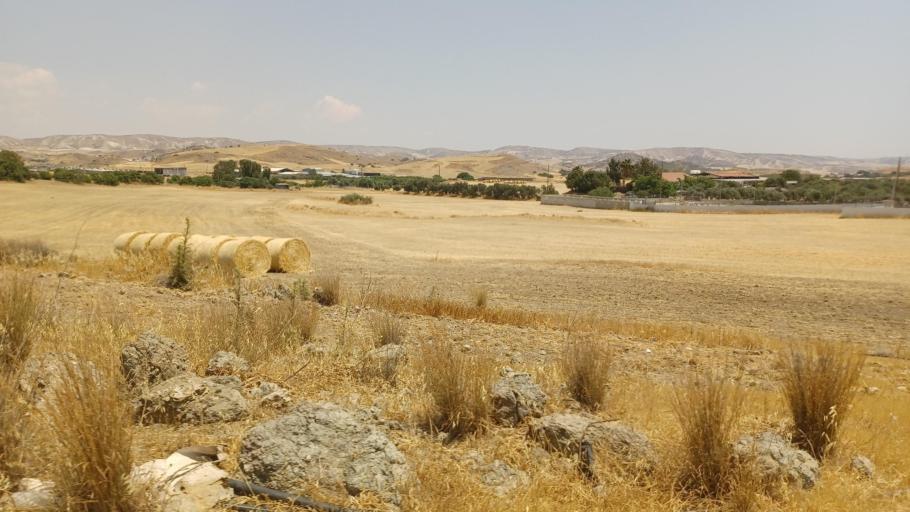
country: CY
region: Larnaka
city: Troulloi
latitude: 35.0138
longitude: 33.6058
